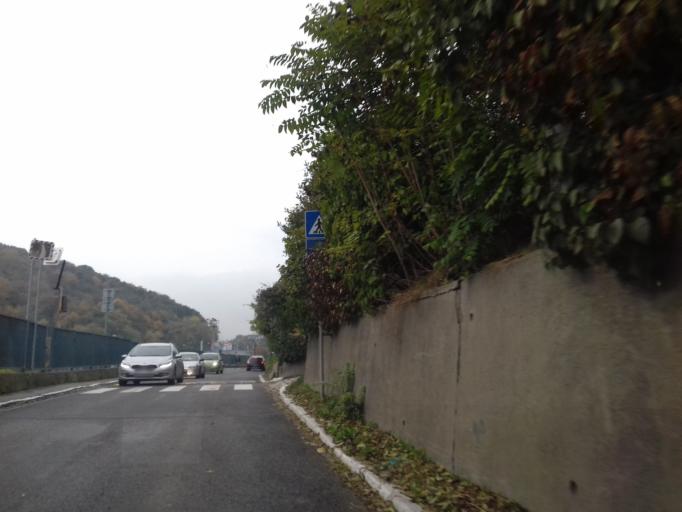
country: SK
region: Bratislavsky
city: Bratislava
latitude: 48.1599
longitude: 17.1061
